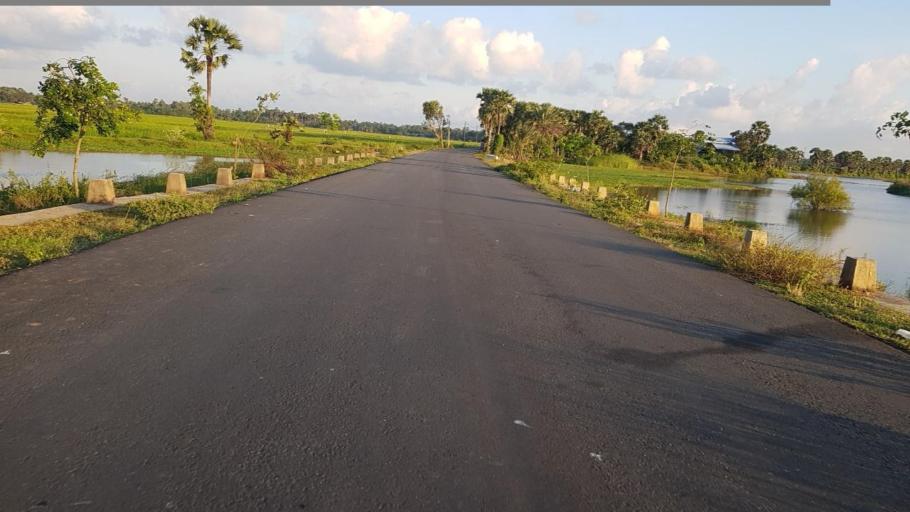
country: LK
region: Northern Province
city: Jaffna
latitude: 9.7274
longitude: 79.9726
